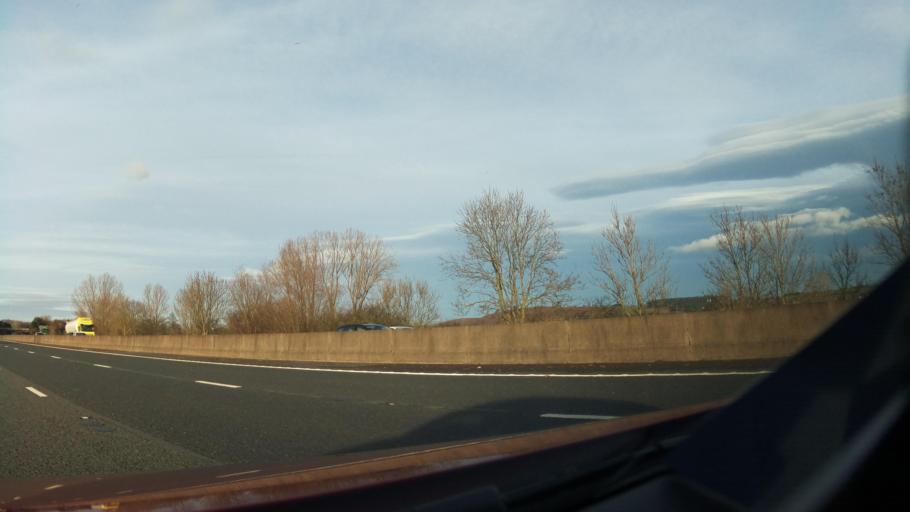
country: GB
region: England
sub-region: Cumbria
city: Penrith
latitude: 54.6867
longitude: -2.7908
